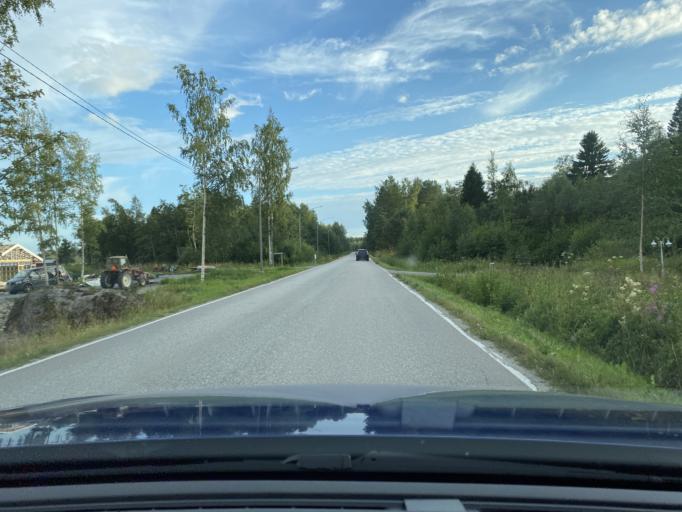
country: FI
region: Ostrobothnia
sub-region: Vaasa
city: Korsnaes
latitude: 62.9580
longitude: 21.1853
